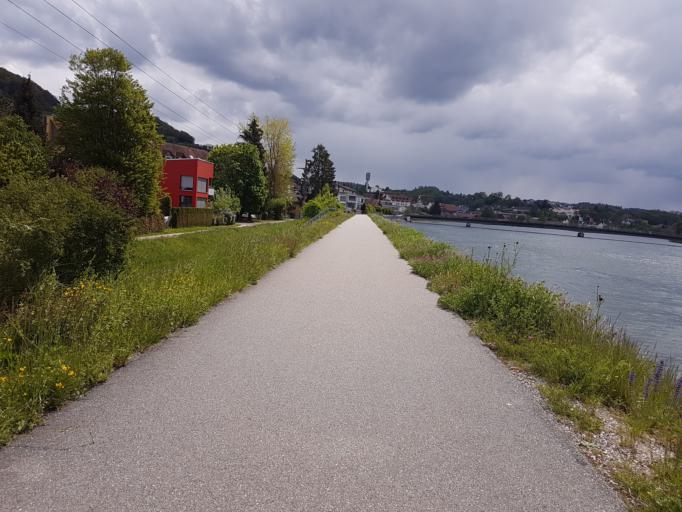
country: CH
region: Aargau
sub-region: Bezirk Zurzach
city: Klingnau
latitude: 47.5757
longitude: 8.2509
